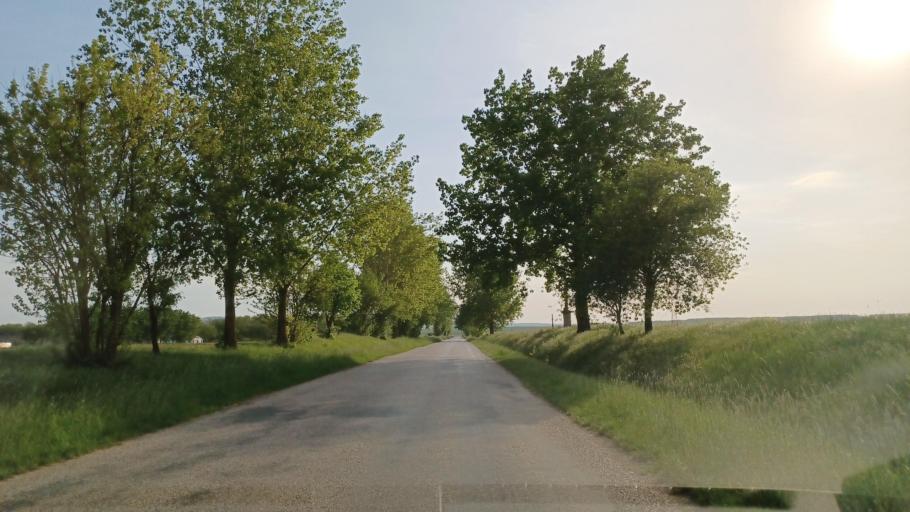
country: HU
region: Baranya
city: Kozarmisleny
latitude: 45.9486
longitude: 18.3683
